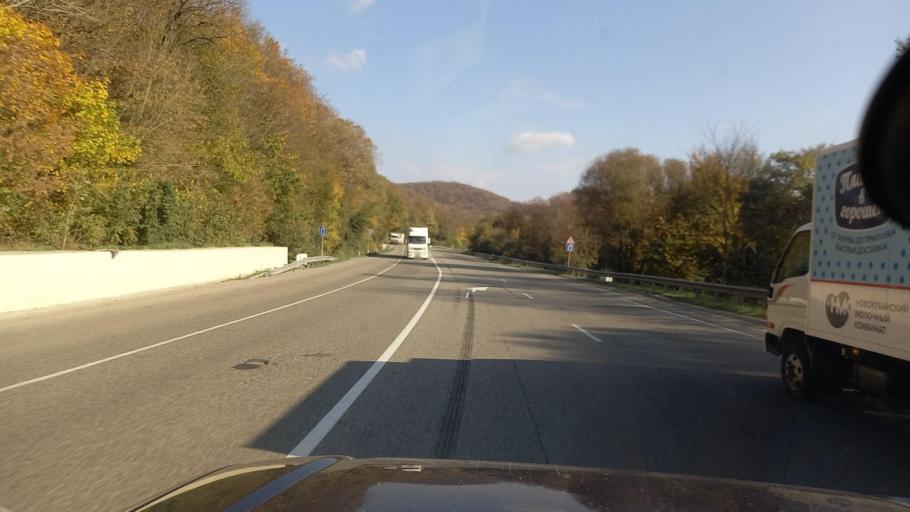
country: RU
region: Krasnodarskiy
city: Verkhnebakanskiy
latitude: 44.8452
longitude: 37.7187
